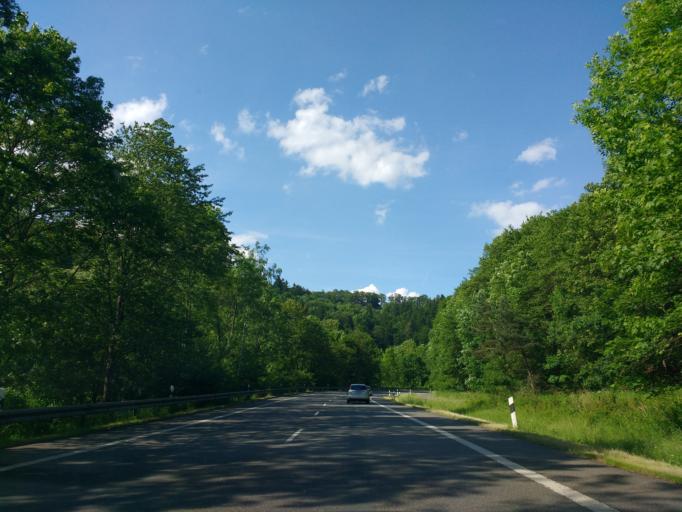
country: DE
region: Hesse
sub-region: Regierungsbezirk Kassel
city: Vohl
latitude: 51.2048
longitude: 8.8906
